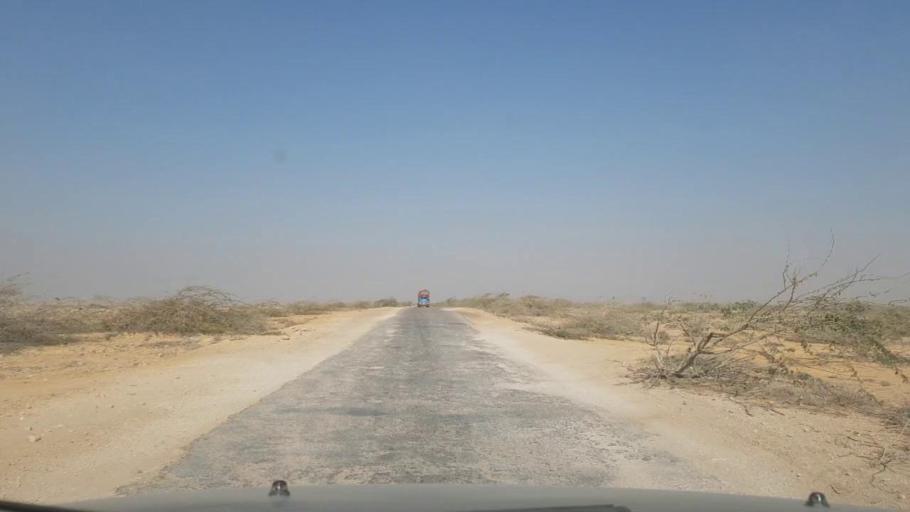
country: PK
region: Sindh
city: Thatta
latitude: 24.8367
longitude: 67.8897
